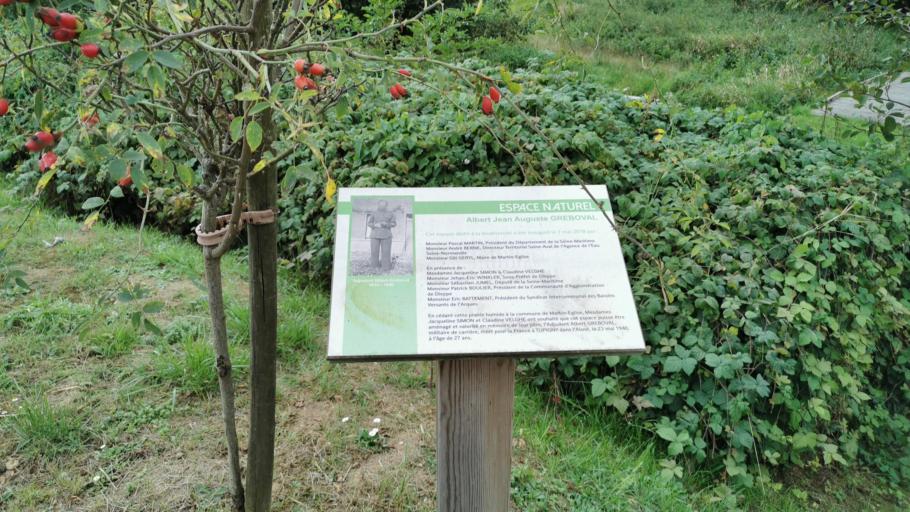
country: FR
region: Haute-Normandie
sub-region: Departement de la Seine-Maritime
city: Martin-Eglise
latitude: 49.8990
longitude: 1.1421
